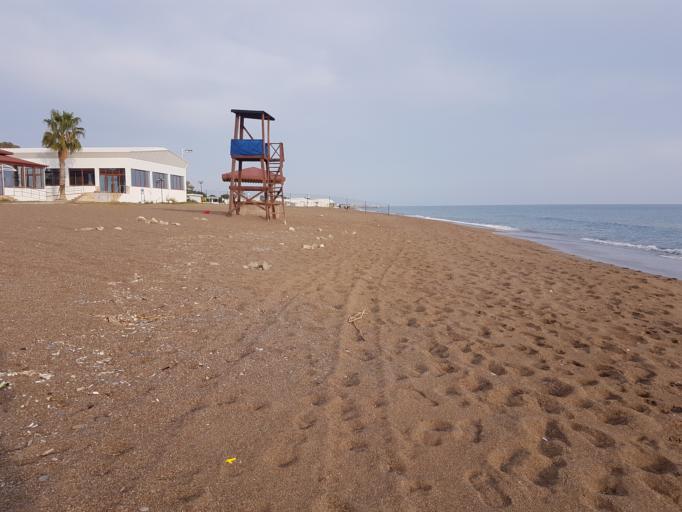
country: TR
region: Antalya
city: Aksu
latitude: 36.8482
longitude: 30.8263
